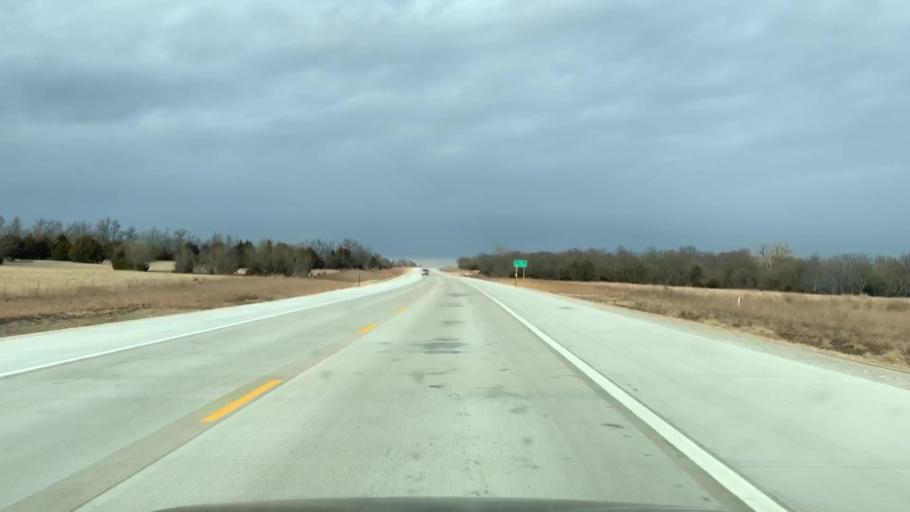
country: US
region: Kansas
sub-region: Allen County
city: Iola
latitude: 37.8649
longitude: -95.4032
